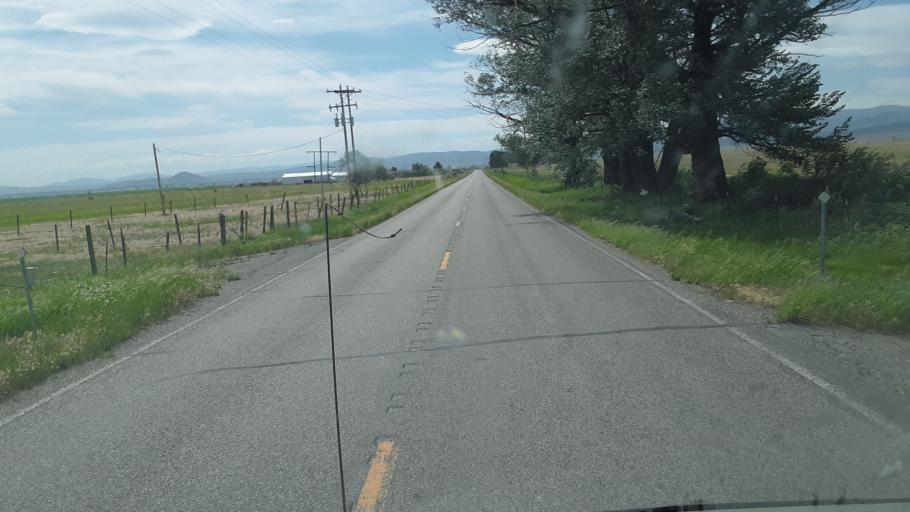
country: US
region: Montana
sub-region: Broadwater County
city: Townsend
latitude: 46.1736
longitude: -111.4634
